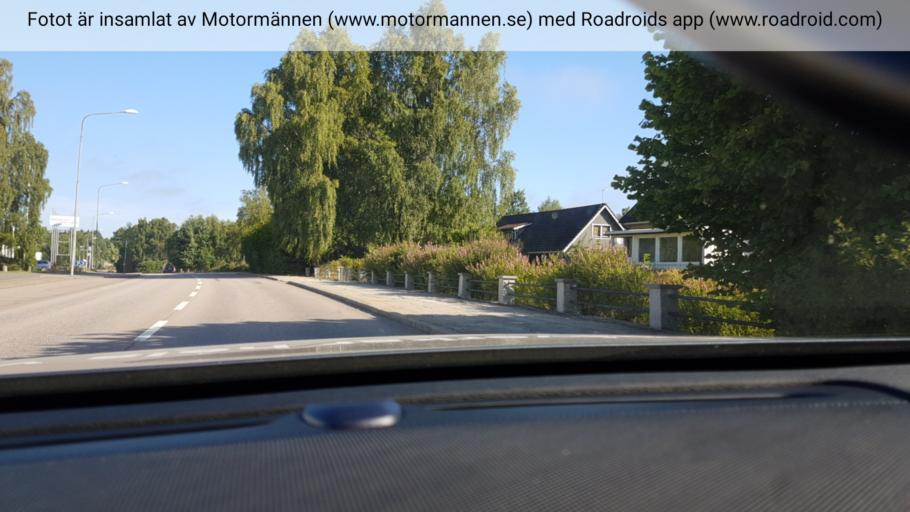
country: SE
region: Skane
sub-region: Hassleholms Kommun
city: Bjarnum
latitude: 56.2995
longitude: 13.7045
